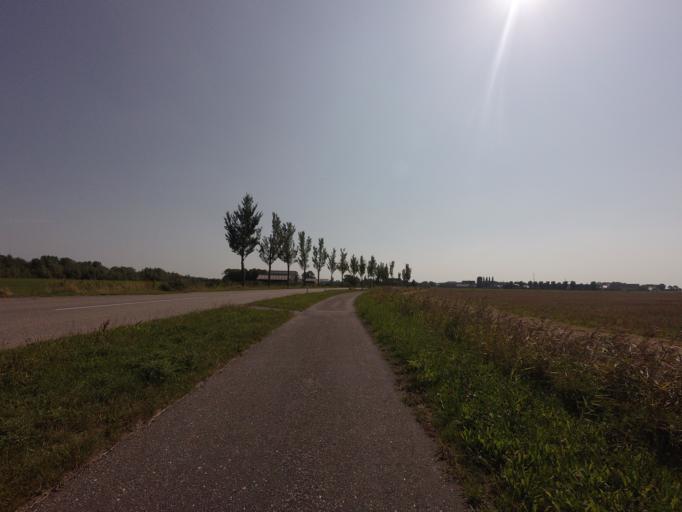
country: NL
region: Groningen
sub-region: Gemeente Zuidhorn
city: Grijpskerk
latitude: 53.2738
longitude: 6.3051
